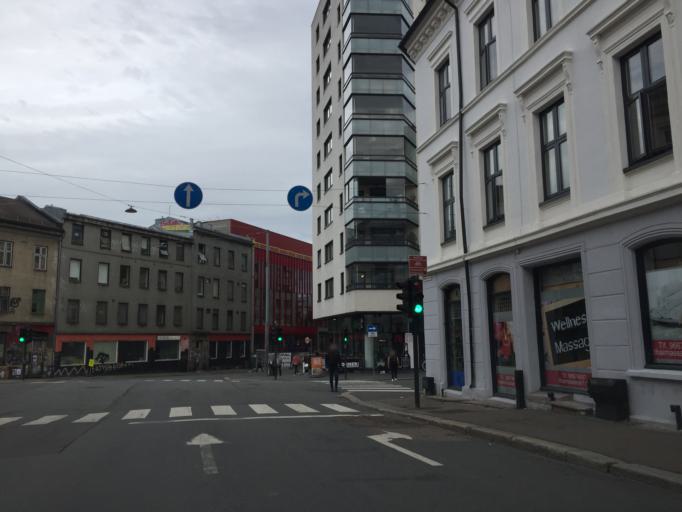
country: NO
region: Oslo
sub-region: Oslo
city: Oslo
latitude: 59.9193
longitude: 10.7508
